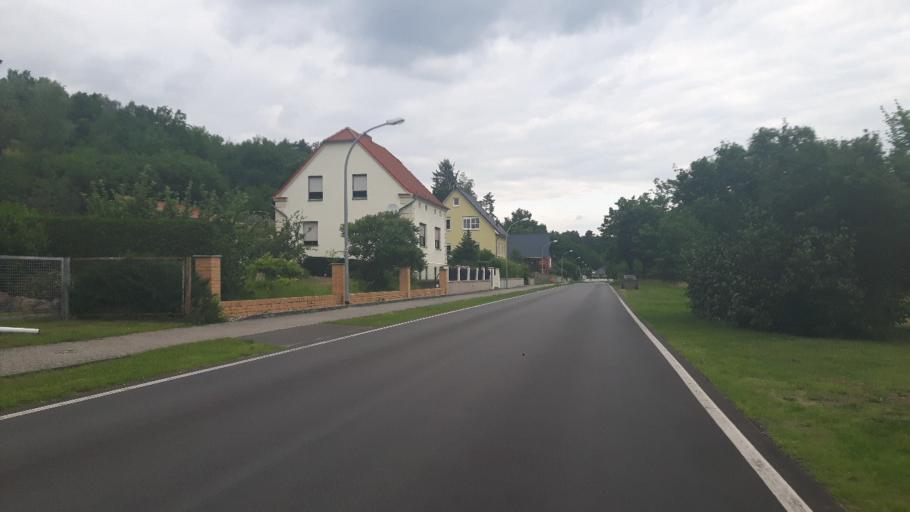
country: DE
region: Brandenburg
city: Niederfinow
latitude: 52.8403
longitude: 13.9374
